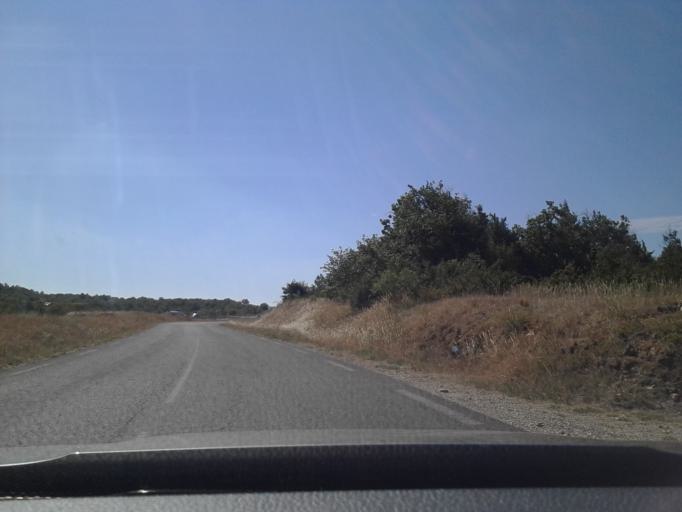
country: FR
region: Midi-Pyrenees
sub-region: Departement de l'Aveyron
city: La Cavalerie
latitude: 43.9270
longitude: 3.2362
